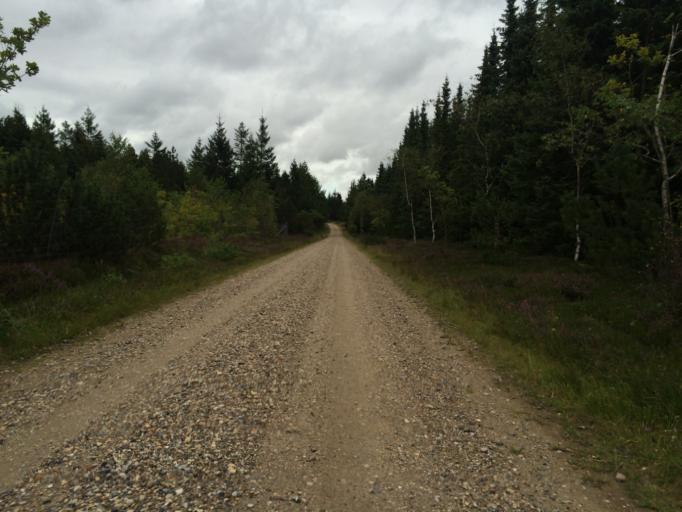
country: DK
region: Central Jutland
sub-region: Holstebro Kommune
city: Ulfborg
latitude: 56.2294
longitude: 8.4144
